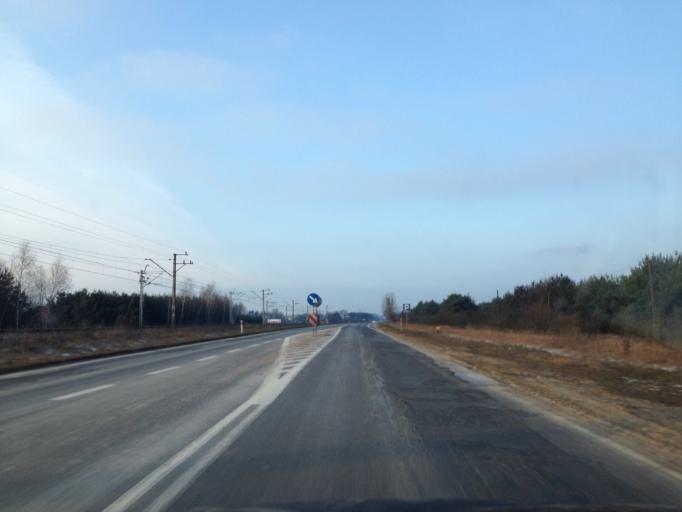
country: PL
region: Greater Poland Voivodeship
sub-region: Powiat poznanski
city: Pobiedziska
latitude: 52.4754
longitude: 17.2490
